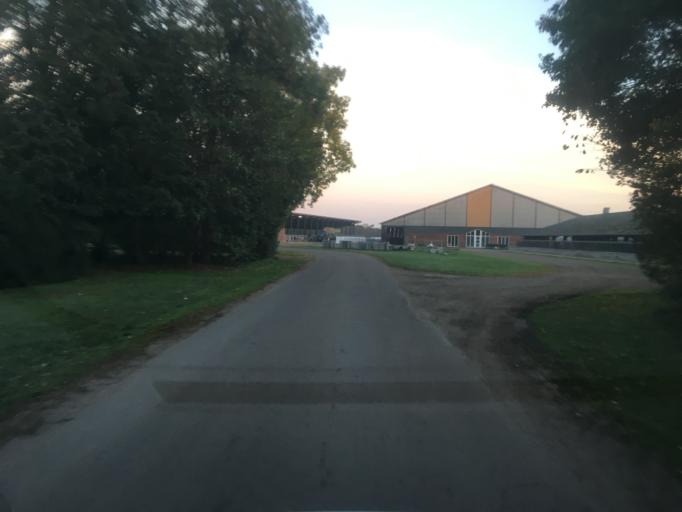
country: DE
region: Schleswig-Holstein
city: Bramstedtlund
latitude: 54.9828
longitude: 9.0654
